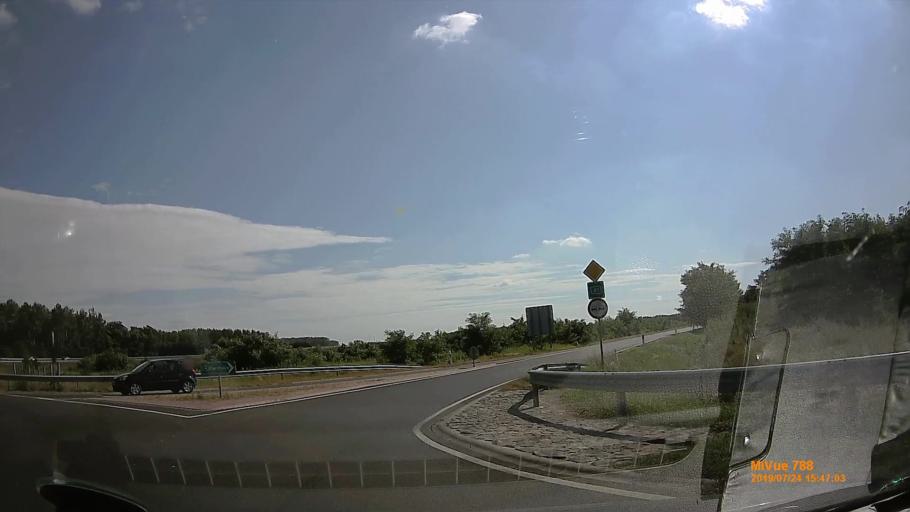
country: HU
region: Szabolcs-Szatmar-Bereg
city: Nagydobos
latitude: 48.0799
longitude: 22.2552
